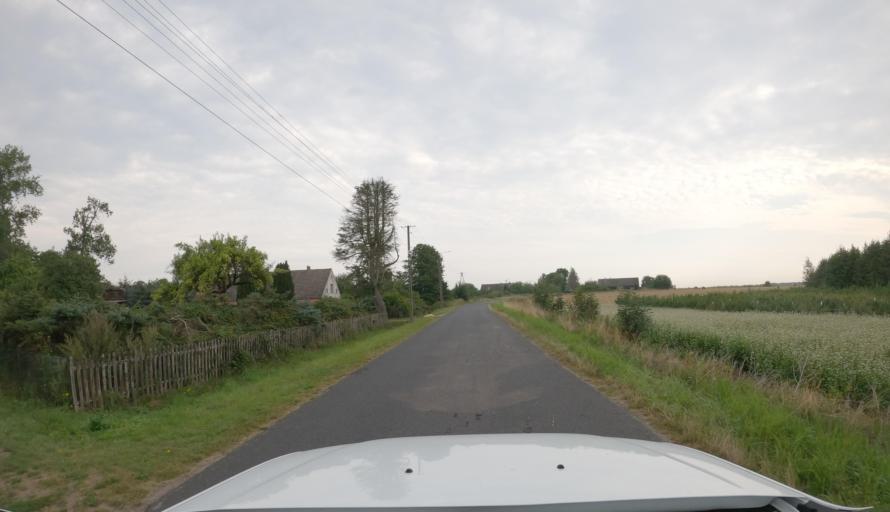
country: PL
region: West Pomeranian Voivodeship
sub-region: Powiat swidwinski
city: Slawoborze
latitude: 53.7989
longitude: 15.6021
